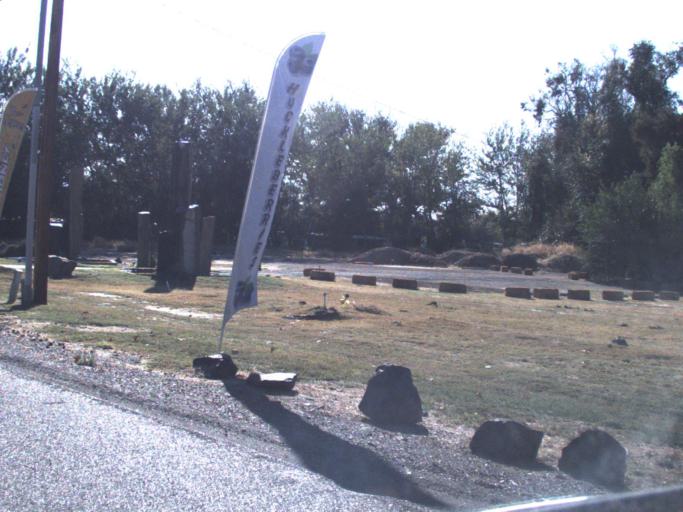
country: US
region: Washington
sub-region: Benton County
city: Richland
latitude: 46.2932
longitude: -119.3183
